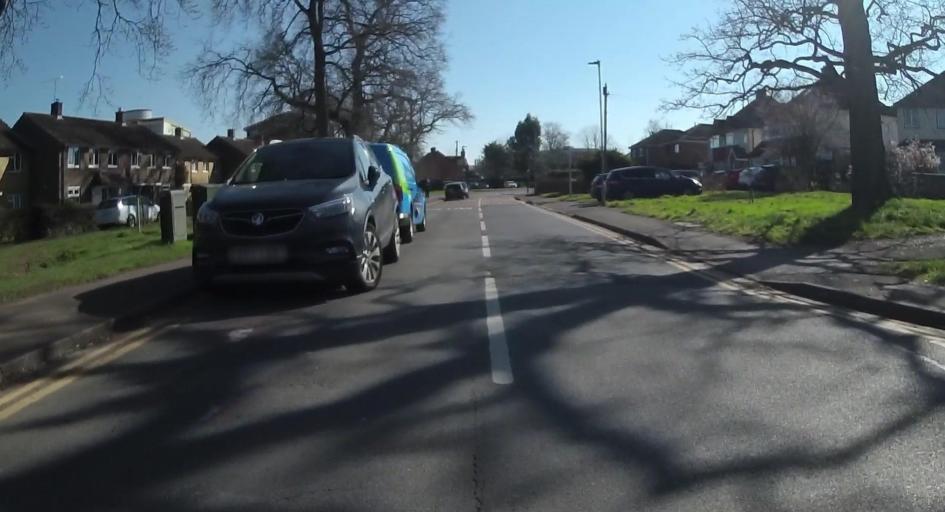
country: GB
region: England
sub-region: Bracknell Forest
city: Bracknell
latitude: 51.4180
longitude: -0.7351
